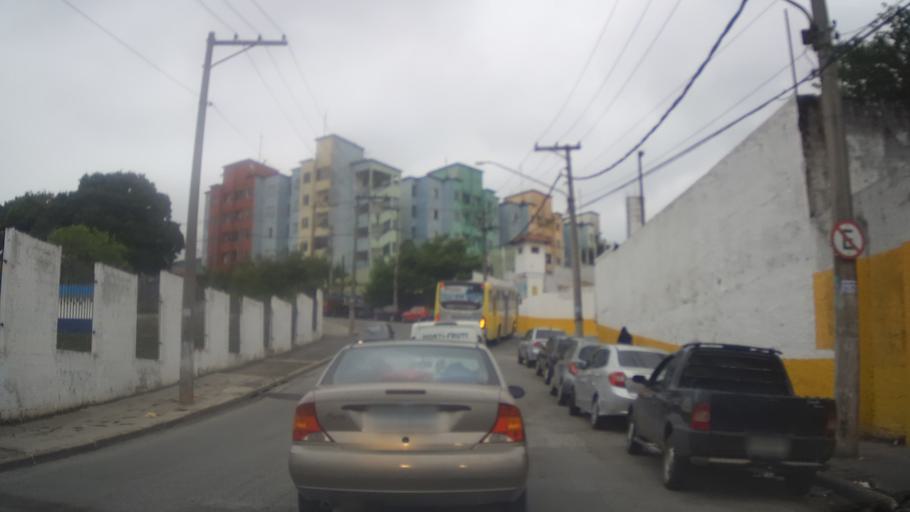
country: BR
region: Sao Paulo
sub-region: Guarulhos
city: Guarulhos
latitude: -23.4409
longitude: -46.5144
